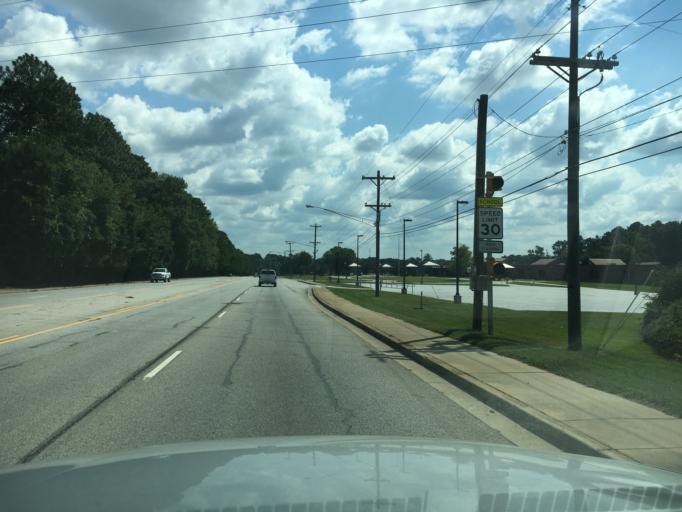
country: US
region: South Carolina
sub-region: Greenwood County
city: Greenwood
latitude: 34.1935
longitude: -82.1880
